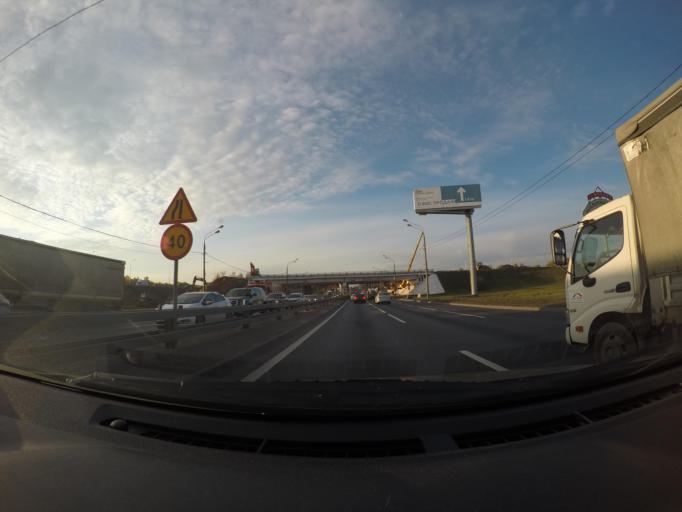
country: RU
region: Moscow
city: Khimki
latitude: 55.9204
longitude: 37.3932
